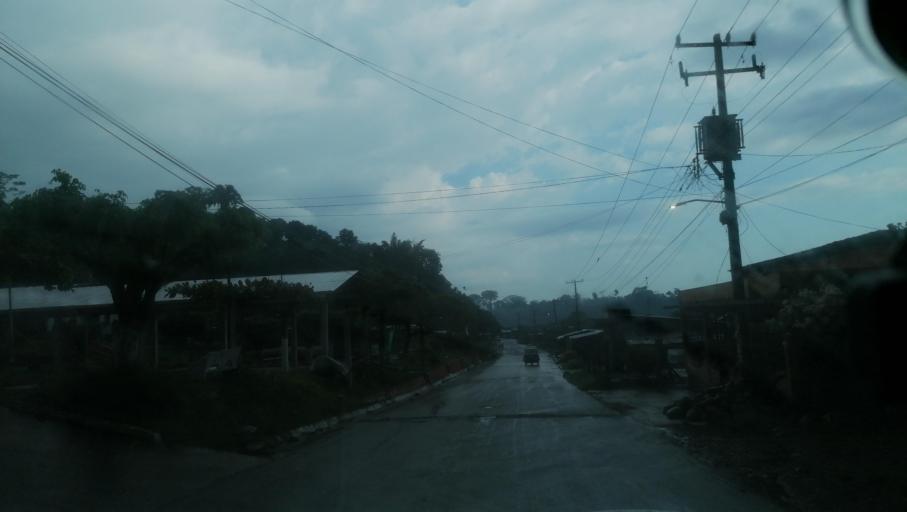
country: MX
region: Chiapas
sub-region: Cacahoatan
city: Benito Juarez
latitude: 15.0557
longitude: -92.1916
